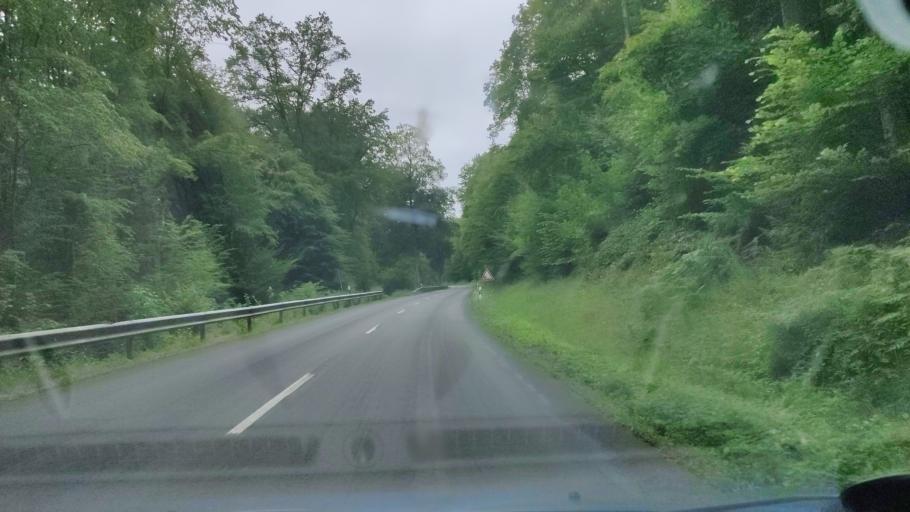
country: DE
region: Lower Saxony
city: Holzminden
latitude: 51.8049
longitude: 9.4795
